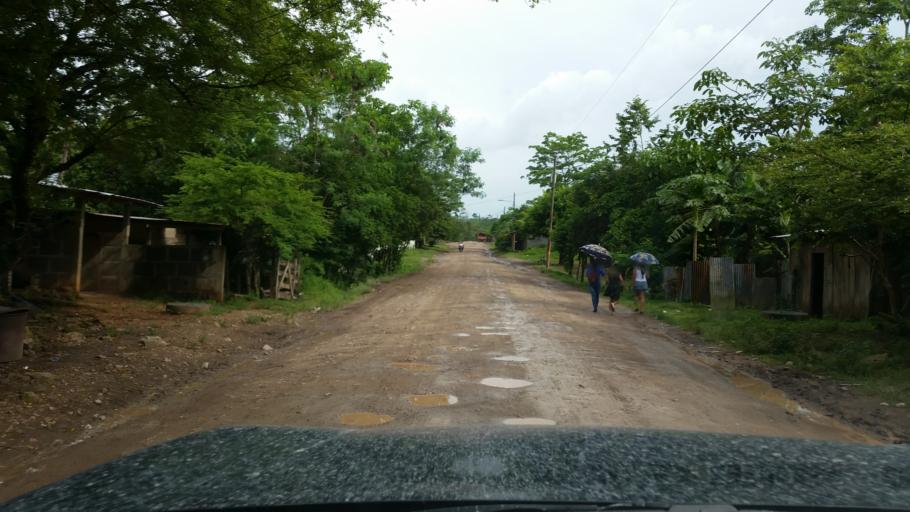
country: NI
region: Atlantico Norte (RAAN)
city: Siuna
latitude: 13.4773
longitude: -84.8439
